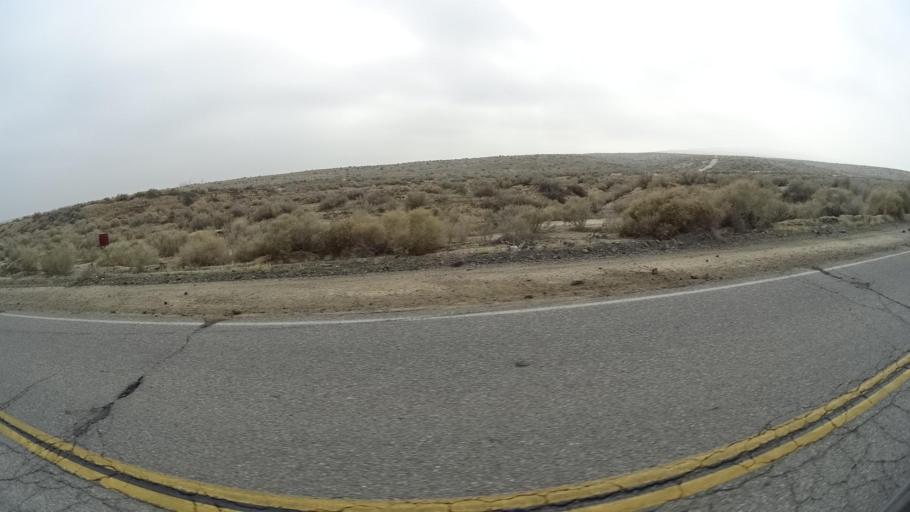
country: US
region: California
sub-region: Kern County
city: South Taft
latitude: 35.1328
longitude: -119.4044
